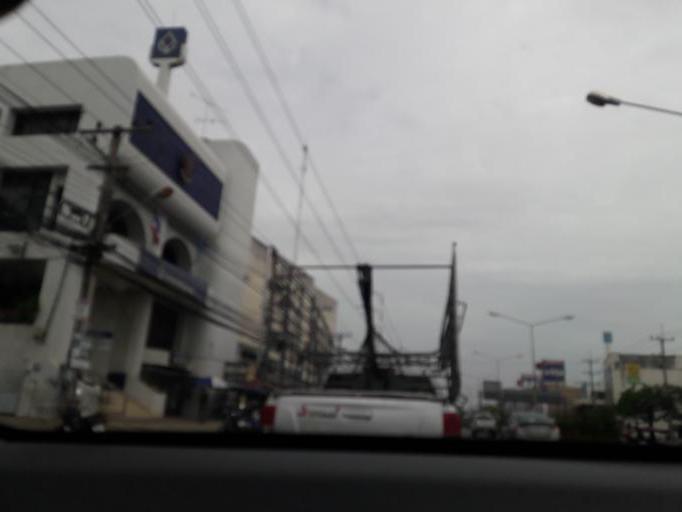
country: TH
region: Ratchaburi
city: Damnoen Saduak
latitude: 13.5313
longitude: 99.9672
